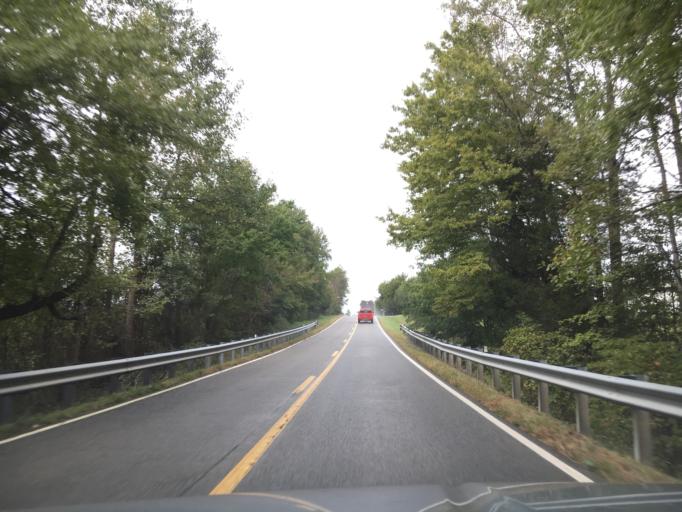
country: US
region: Virginia
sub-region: Goochland County
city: Goochland
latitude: 37.7571
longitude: -77.8695
